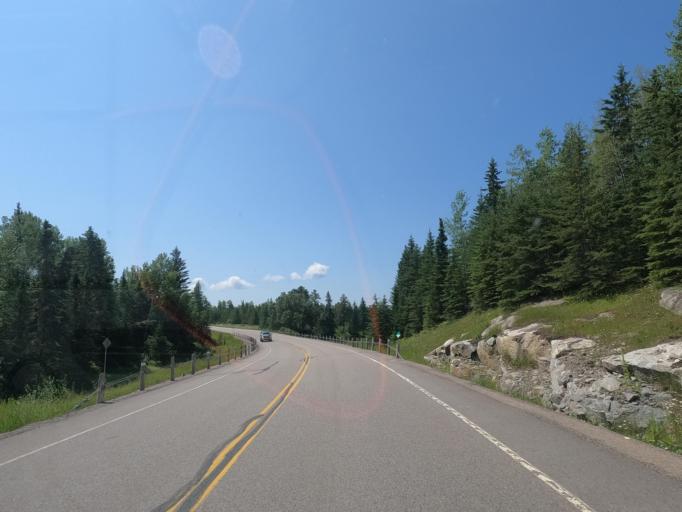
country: CA
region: Ontario
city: Dryden
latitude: 49.8995
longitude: -93.3673
